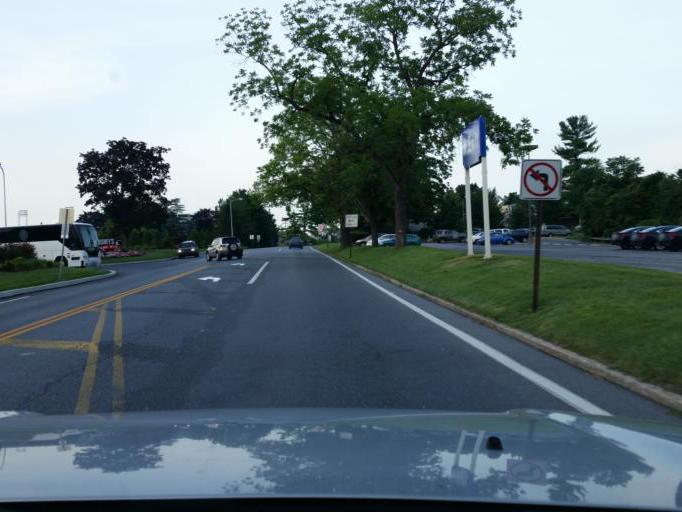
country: US
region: Pennsylvania
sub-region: Dauphin County
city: Hershey
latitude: 40.2861
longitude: -76.6627
